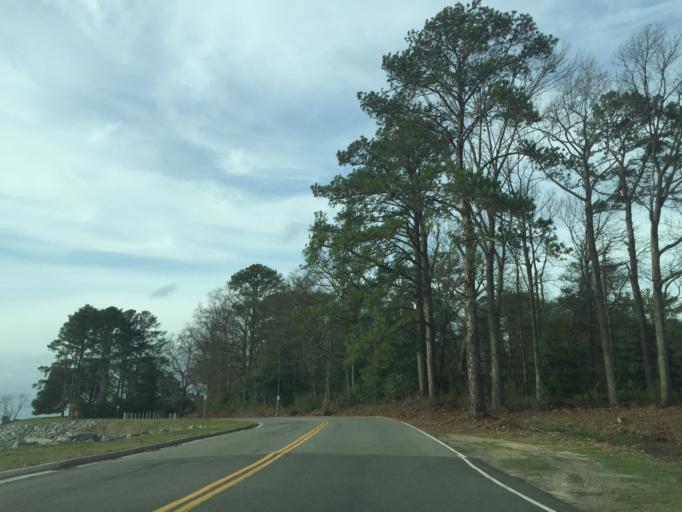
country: US
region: Virginia
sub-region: City of Newport News
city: Newport News
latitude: 37.0421
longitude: -76.4895
